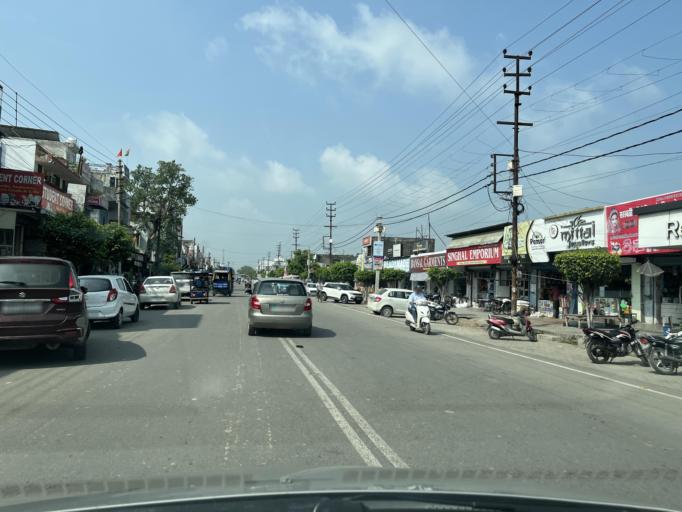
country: IN
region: Uttarakhand
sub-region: Udham Singh Nagar
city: Bazpur
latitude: 29.1605
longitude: 79.1532
